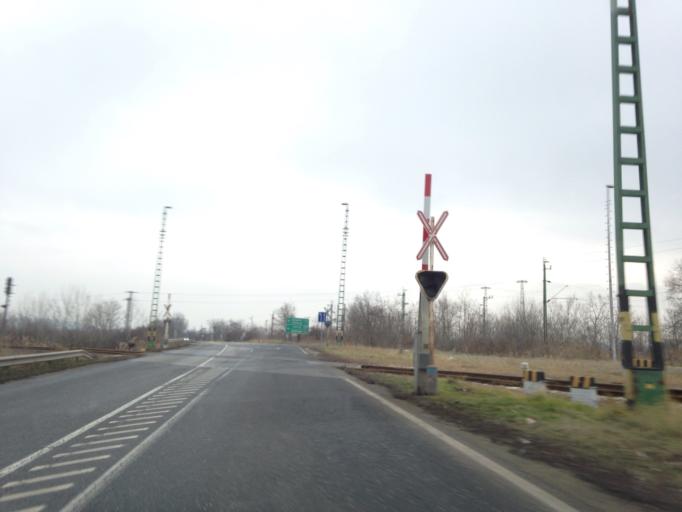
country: HU
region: Komarom-Esztergom
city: Almasfuzito
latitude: 47.7216
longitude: 18.2707
